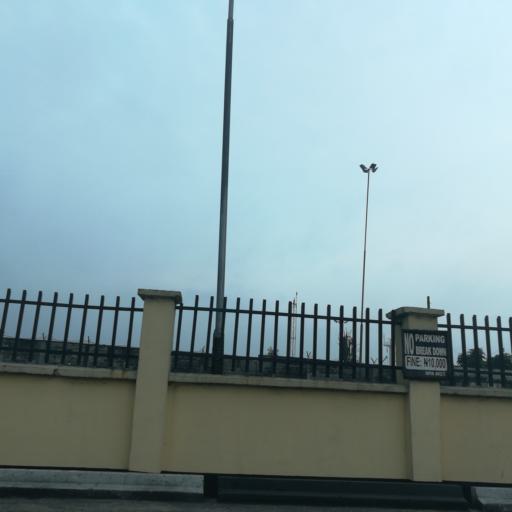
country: NG
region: Rivers
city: Port Harcourt
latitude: 4.7687
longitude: 7.0110
